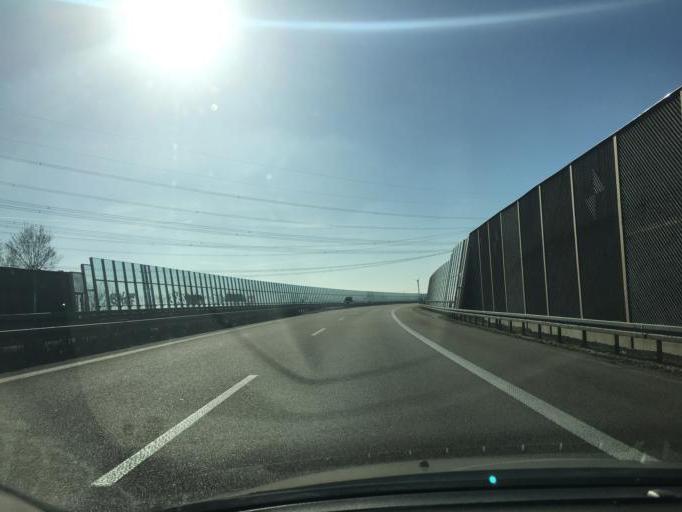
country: DE
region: Saxony
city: Hartmannsdorf
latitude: 50.8653
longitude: 12.8128
